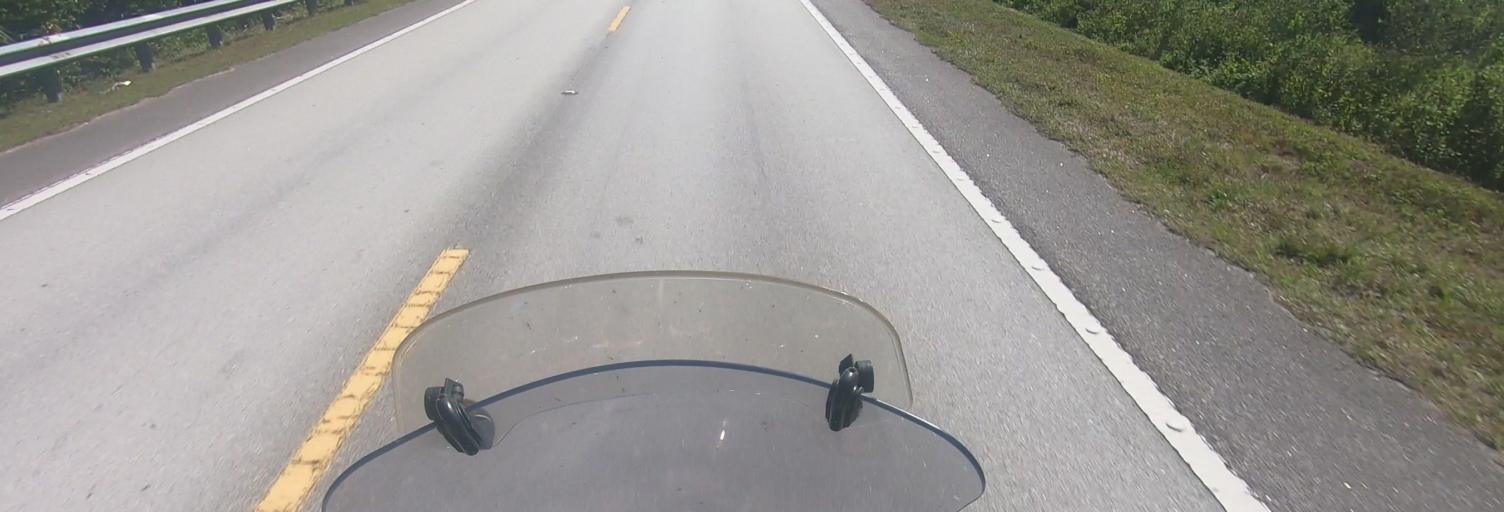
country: US
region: Florida
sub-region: Collier County
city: Marco
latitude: 25.8688
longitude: -81.1713
